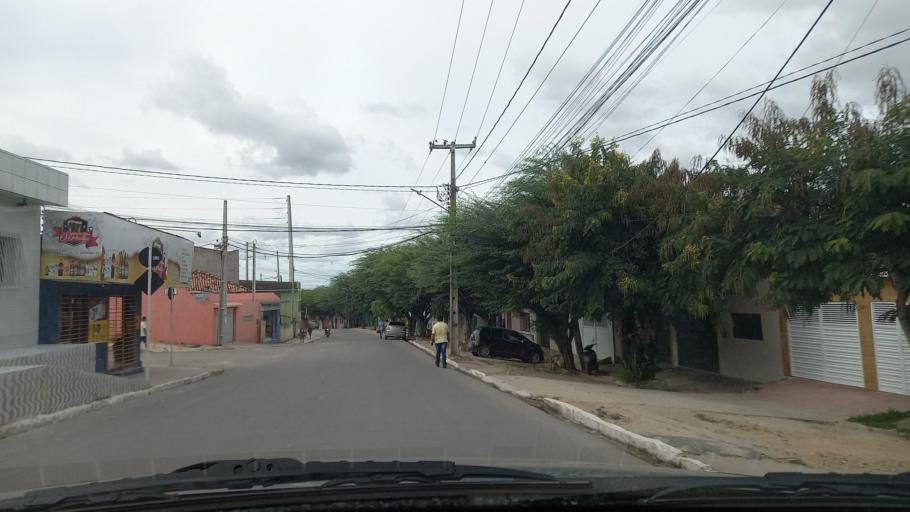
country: BR
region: Pernambuco
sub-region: Gravata
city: Gravata
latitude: -8.2079
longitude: -35.5701
